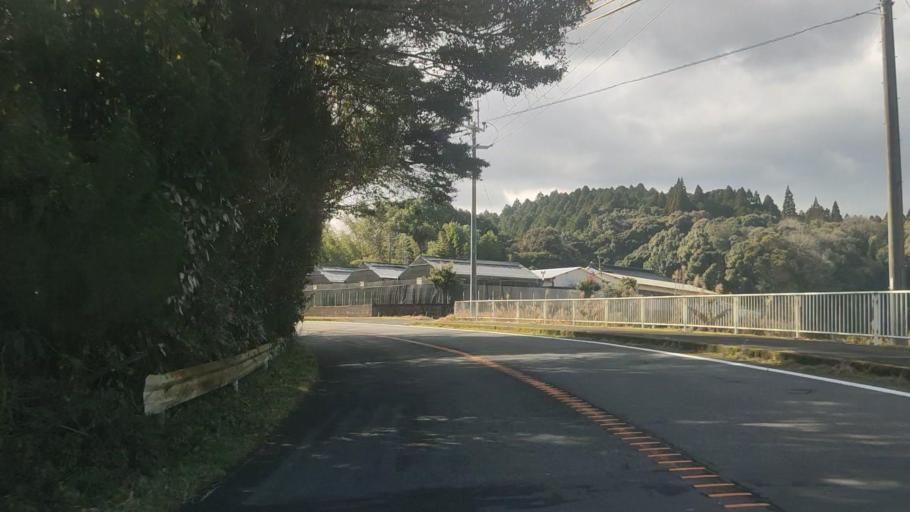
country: JP
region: Kagoshima
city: Okuchi-shinohara
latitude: 31.9382
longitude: 130.7061
